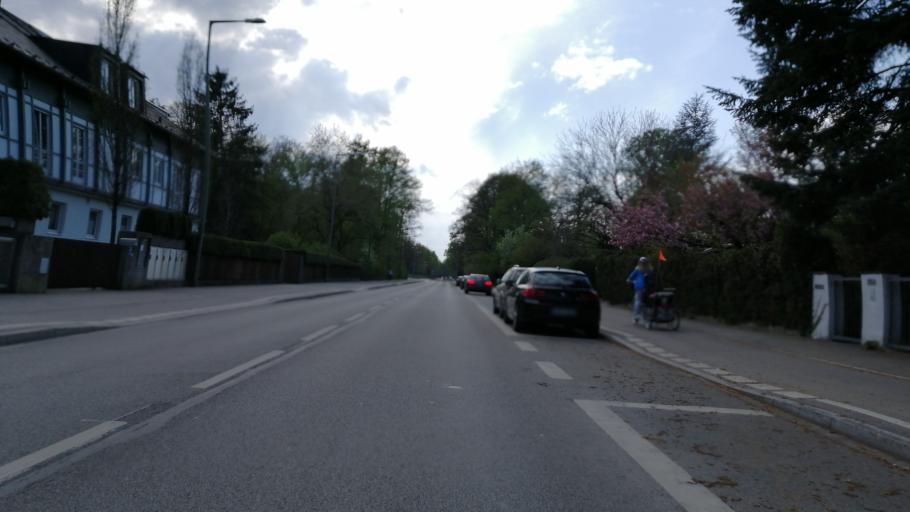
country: DE
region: Bavaria
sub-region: Upper Bavaria
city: Unterhaching
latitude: 48.0873
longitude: 11.6027
